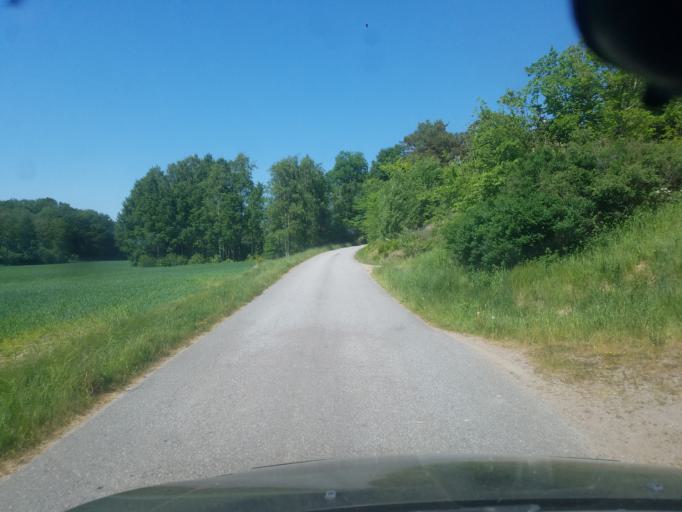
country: SE
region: Vaestra Goetaland
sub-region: Orust
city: Henan
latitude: 58.2675
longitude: 11.5732
